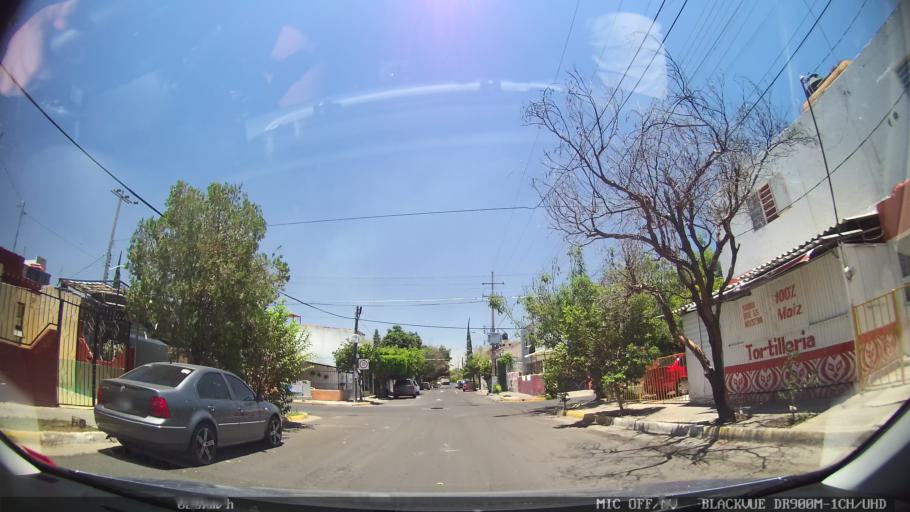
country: MX
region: Jalisco
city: Tlaquepaque
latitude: 20.6767
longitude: -103.2825
